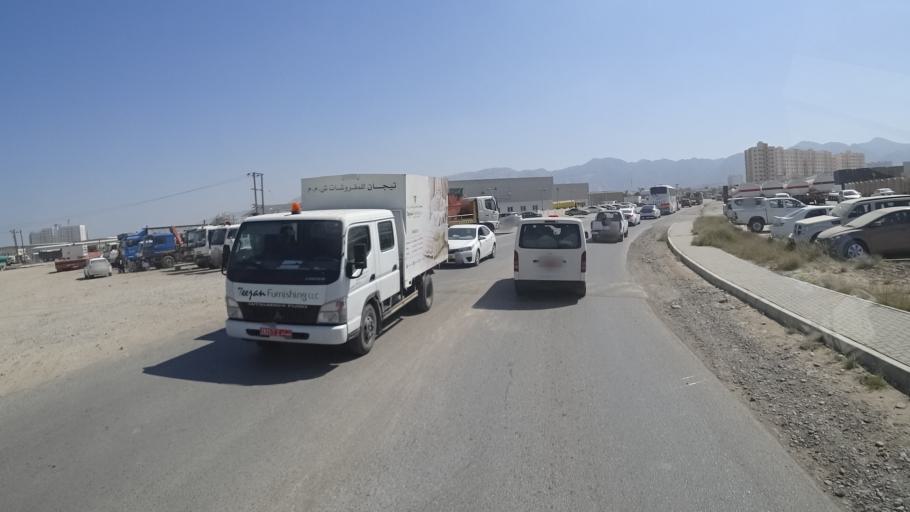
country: OM
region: Muhafazat Masqat
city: Bawshar
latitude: 23.5798
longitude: 58.3642
